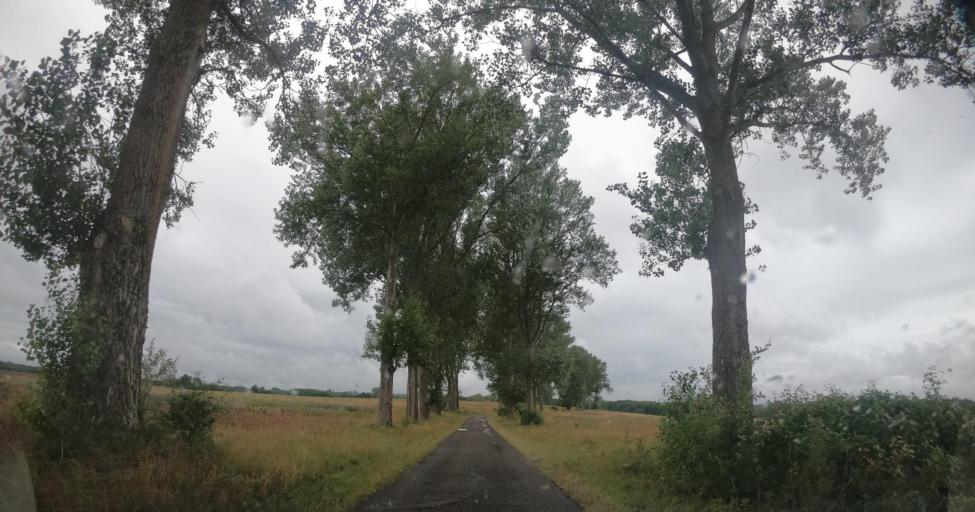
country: PL
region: West Pomeranian Voivodeship
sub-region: Powiat lobeski
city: Wegorzyno
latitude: 53.5367
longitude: 15.5120
